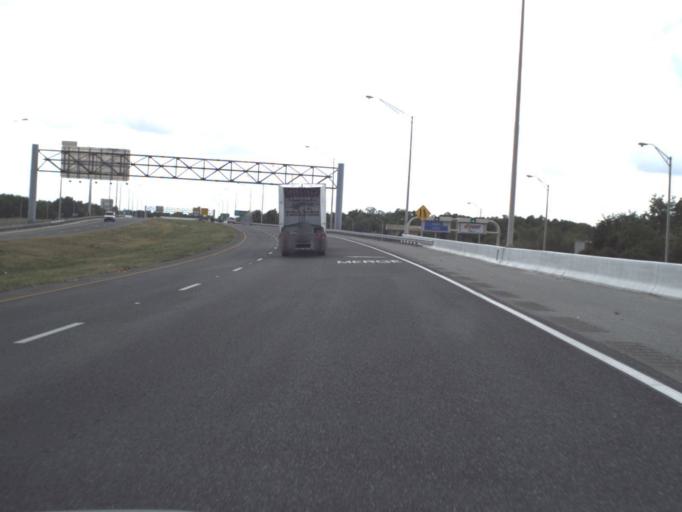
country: US
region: Florida
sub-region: Orange County
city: Paradise Heights
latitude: 28.6370
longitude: -81.5438
